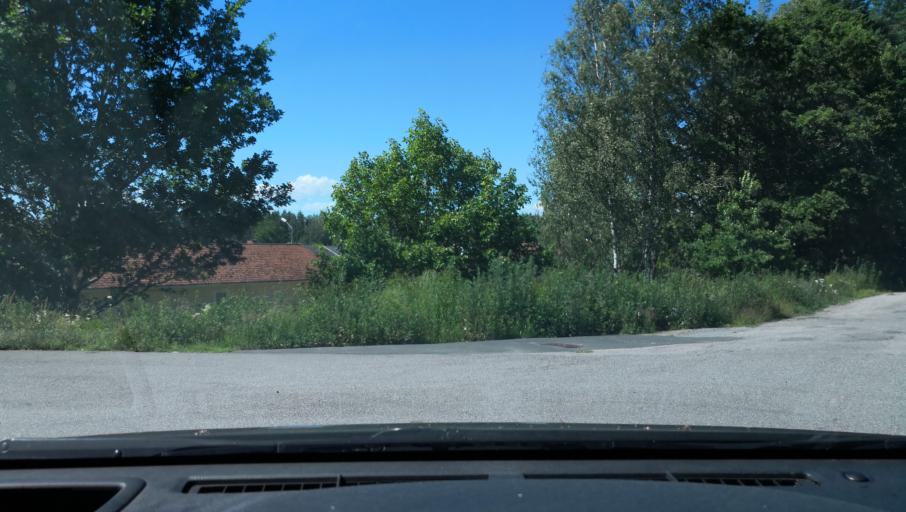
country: SE
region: Vaestmanland
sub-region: Kungsors Kommun
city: Kungsoer
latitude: 59.2793
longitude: 16.1186
